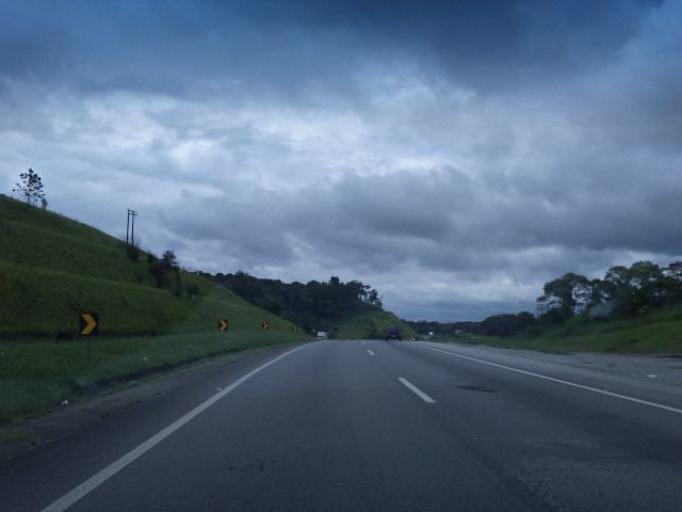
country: BR
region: Sao Paulo
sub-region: Juquitiba
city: Juquitiba
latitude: -23.9741
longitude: -47.1385
